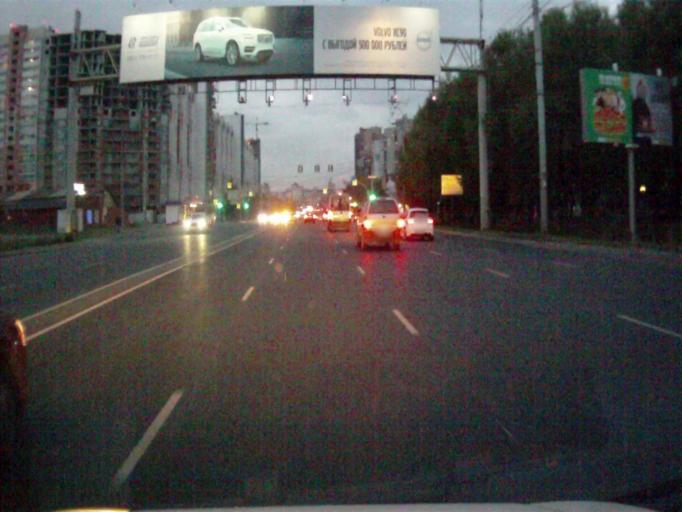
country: RU
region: Chelyabinsk
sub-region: Gorod Chelyabinsk
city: Chelyabinsk
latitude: 55.1772
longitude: 61.3131
